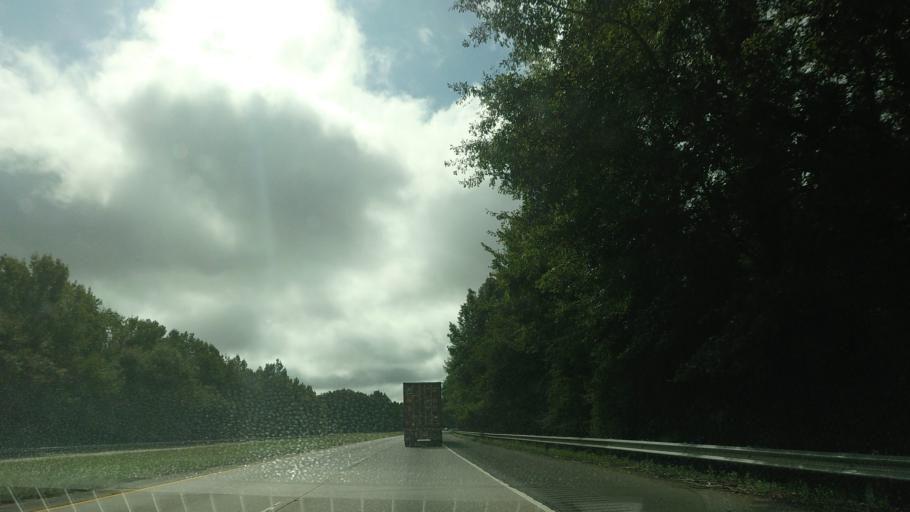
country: US
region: Georgia
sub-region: Bibb County
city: Macon
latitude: 32.8141
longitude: -83.5805
